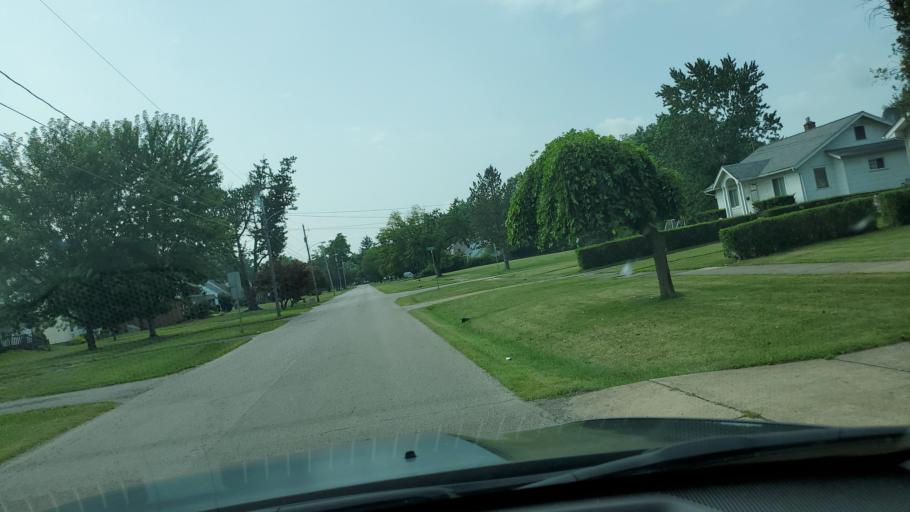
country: US
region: Ohio
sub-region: Trumbull County
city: Bolindale
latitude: 41.2304
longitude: -80.7814
